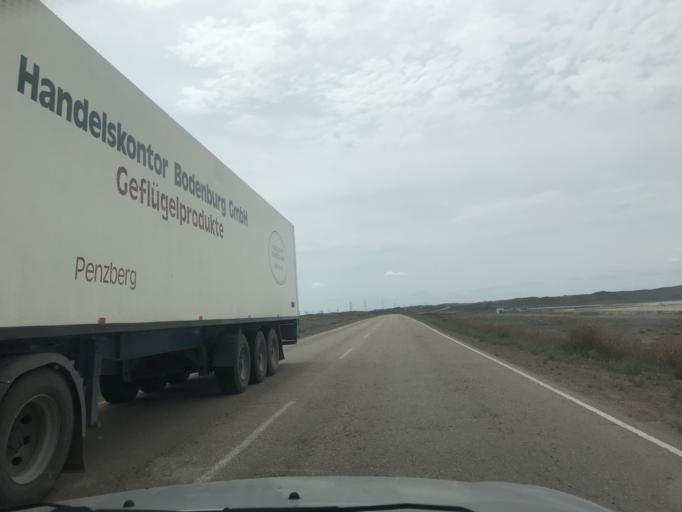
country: KZ
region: Zhambyl
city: Mynaral
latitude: 45.3976
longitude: 73.6410
